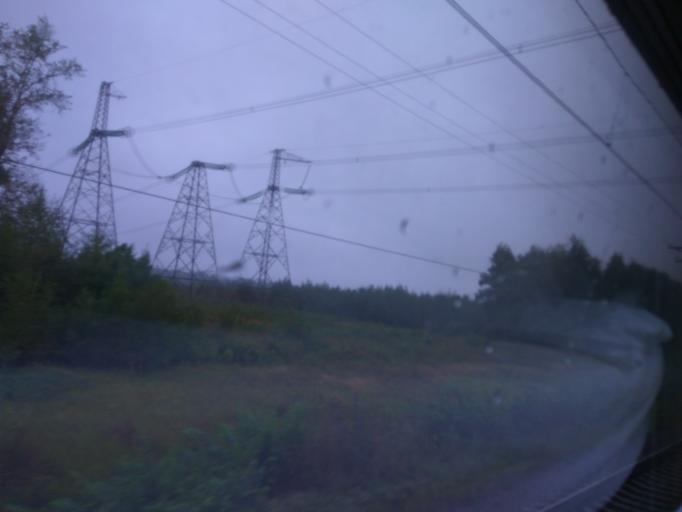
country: RU
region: Moskovskaya
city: Ozherel'ye
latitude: 54.7544
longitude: 38.3380
